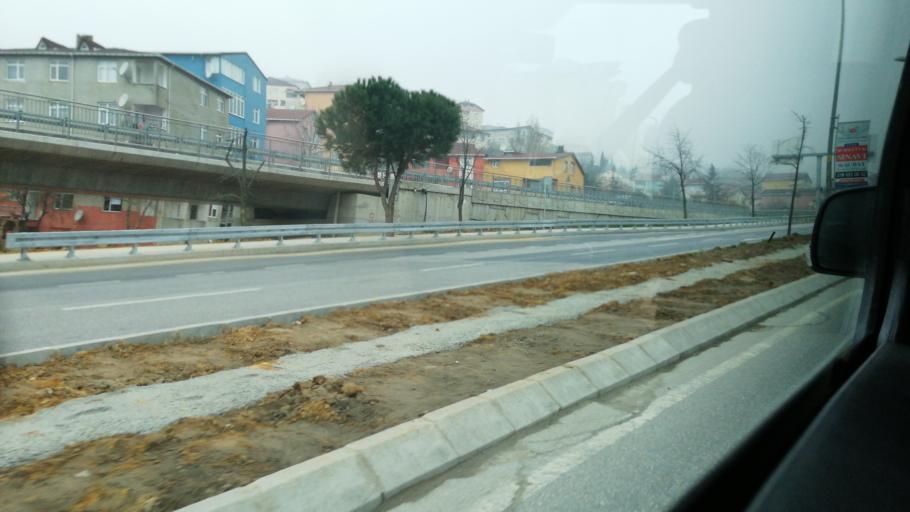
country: TR
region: Istanbul
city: Umraniye
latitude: 41.0858
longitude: 29.0858
